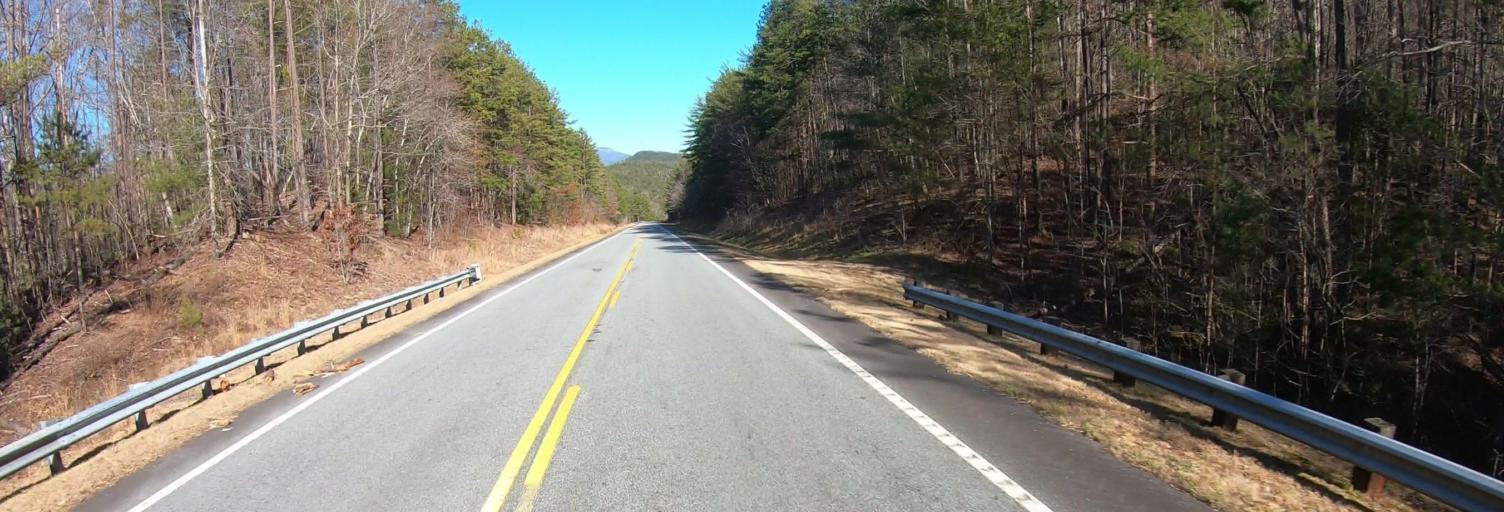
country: US
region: South Carolina
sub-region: Pickens County
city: Pickens
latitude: 34.9417
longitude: -82.8653
